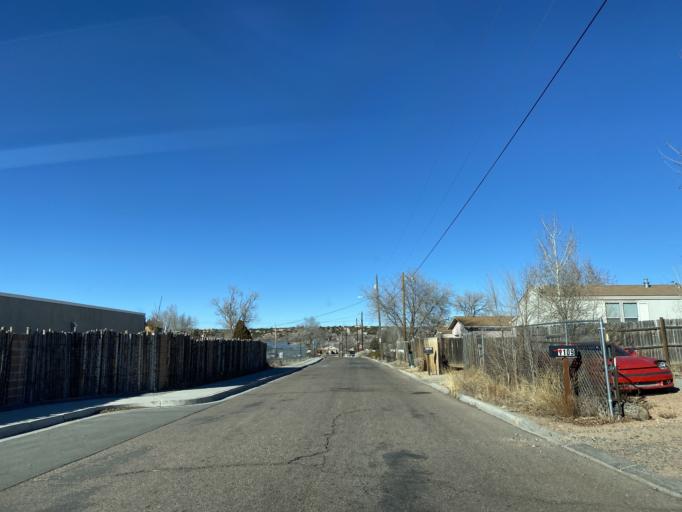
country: US
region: New Mexico
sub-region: Santa Fe County
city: Agua Fria
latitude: 35.6655
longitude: -105.9898
